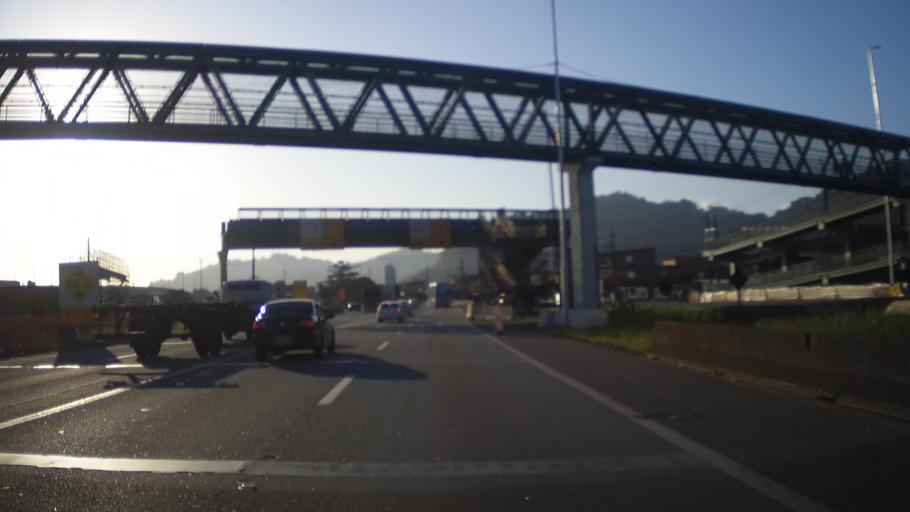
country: BR
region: Sao Paulo
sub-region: Sao Vicente
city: Sao Vicente
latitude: -23.9293
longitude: -46.3658
